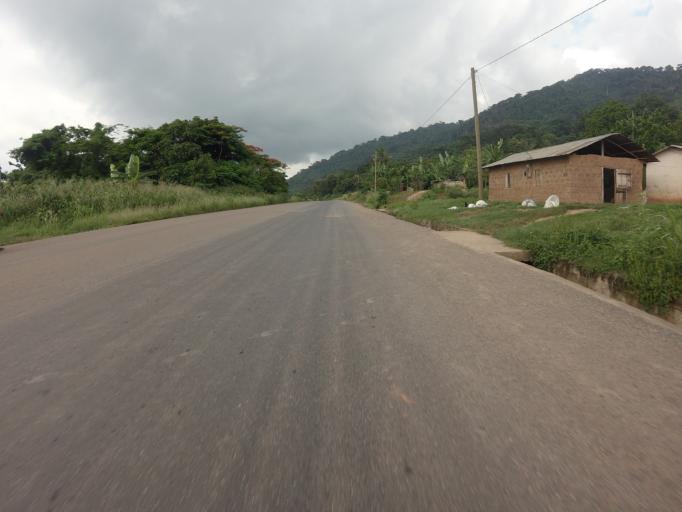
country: GH
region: Volta
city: Kpandu
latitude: 6.9133
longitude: 0.4513
